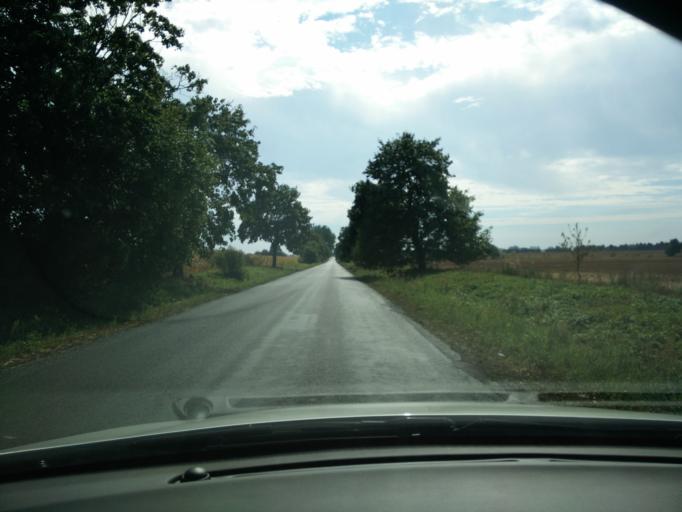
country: PL
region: Greater Poland Voivodeship
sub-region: Powiat sredzki
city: Sroda Wielkopolska
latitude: 52.2696
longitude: 17.2213
